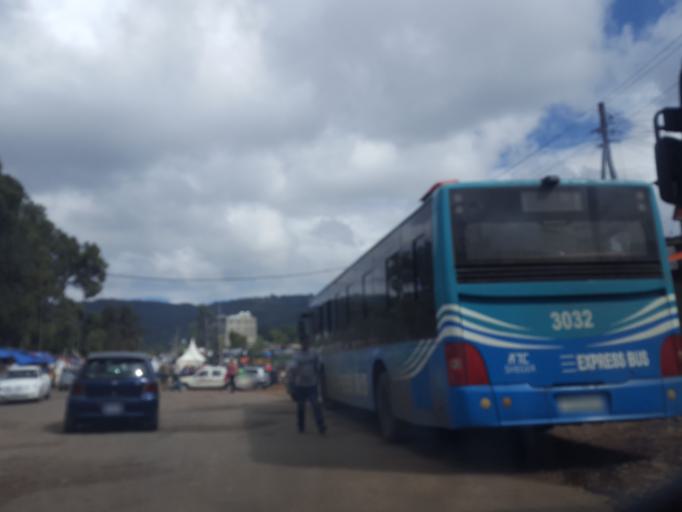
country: ET
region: Adis Abeba
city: Addis Ababa
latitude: 9.0625
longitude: 38.7613
